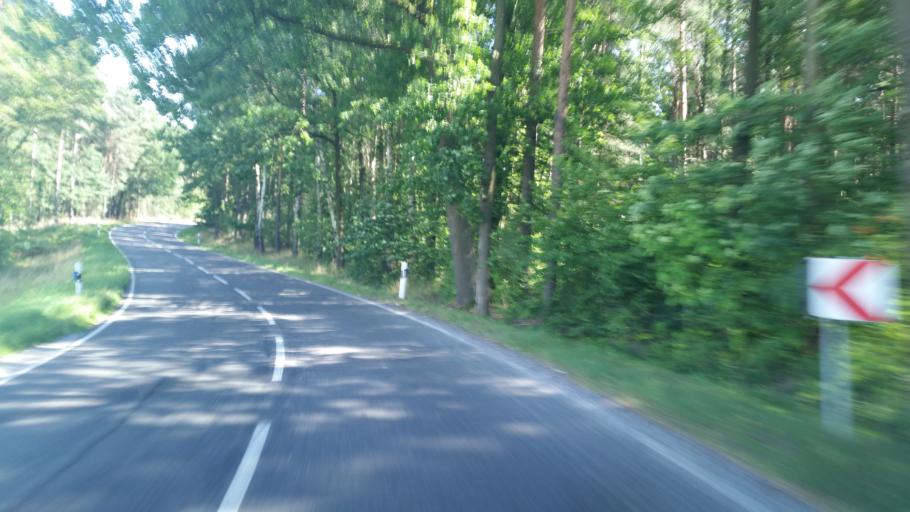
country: DE
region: Saxony
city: Neukirch
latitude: 51.3056
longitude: 14.0411
